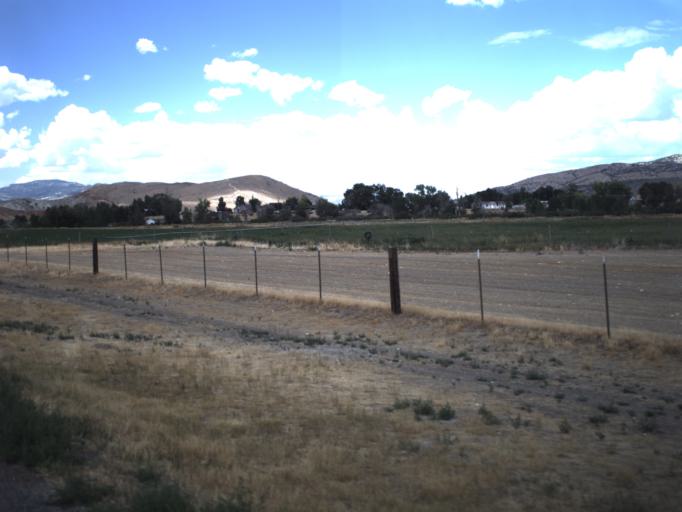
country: US
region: Utah
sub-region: Sanpete County
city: Centerfield
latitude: 39.1202
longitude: -111.7137
